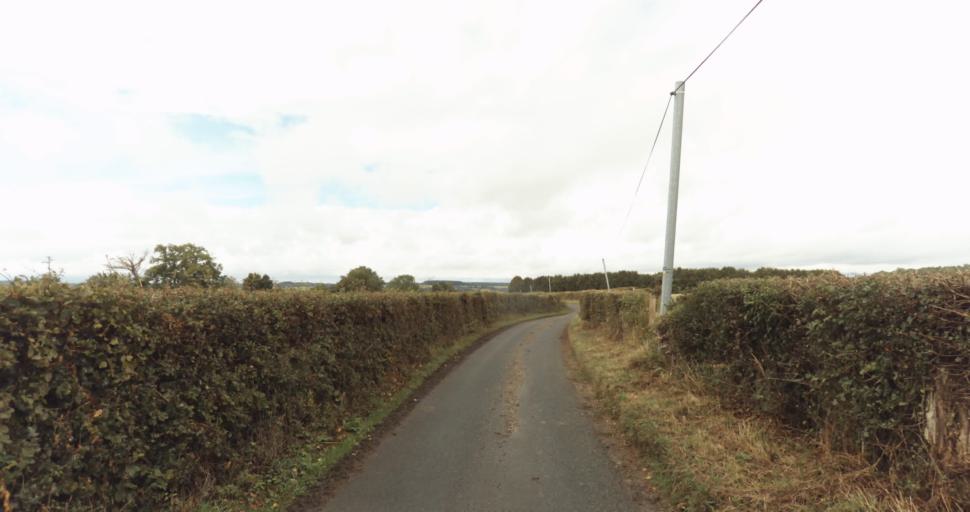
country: FR
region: Lower Normandy
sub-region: Departement de l'Orne
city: Vimoutiers
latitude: 48.8604
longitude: 0.1697
